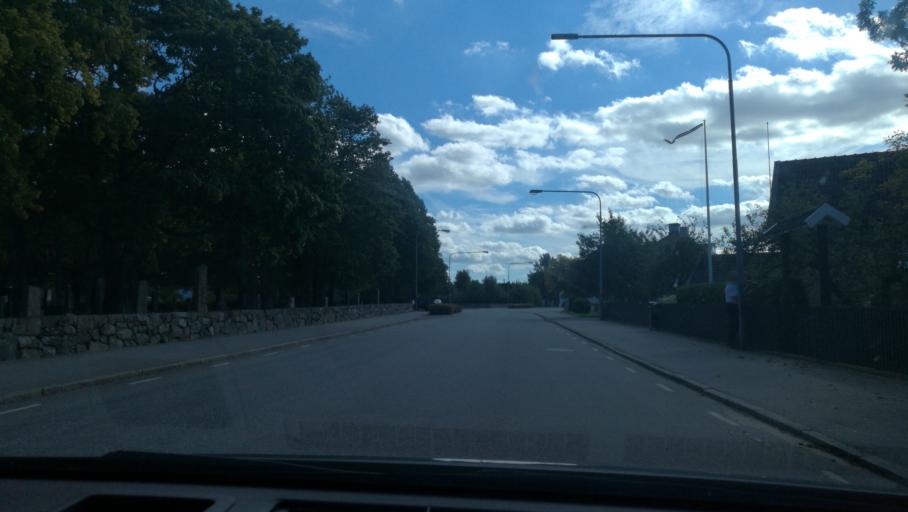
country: SE
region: Vaestra Goetaland
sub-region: Mariestads Kommun
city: Mariestad
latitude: 58.7023
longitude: 13.8358
